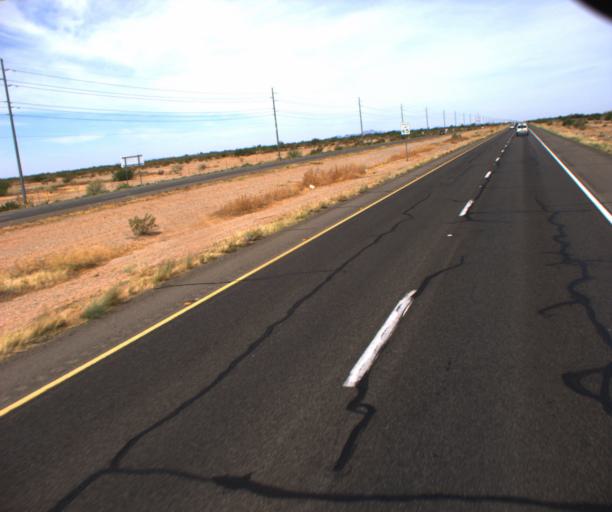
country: US
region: Arizona
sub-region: Maricopa County
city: Sun City West
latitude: 33.7159
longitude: -112.4489
